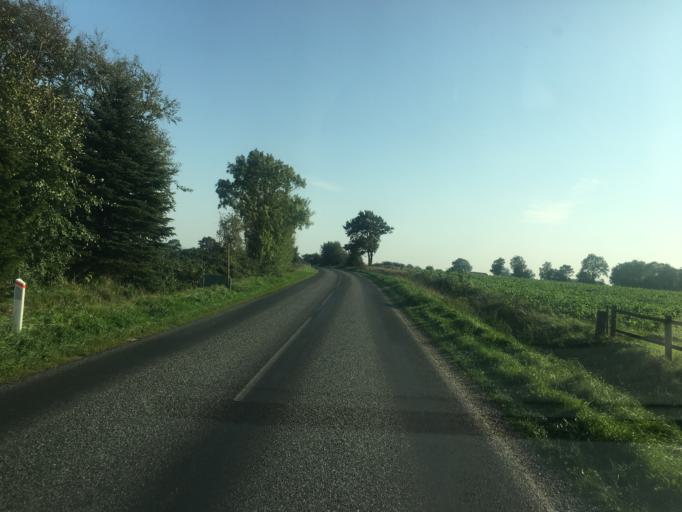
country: DE
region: Schleswig-Holstein
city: Bramstedtlund
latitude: 54.9570
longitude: 9.0535
